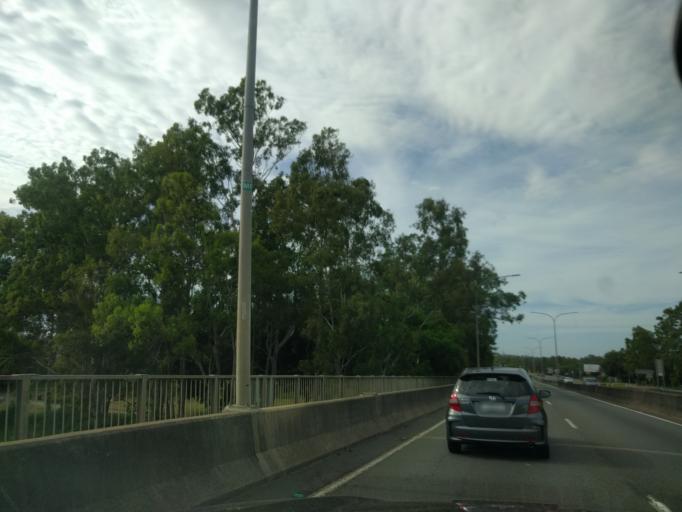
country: AU
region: Queensland
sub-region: Brisbane
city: Seventeen Mile Rocks
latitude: -27.5282
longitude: 152.9470
